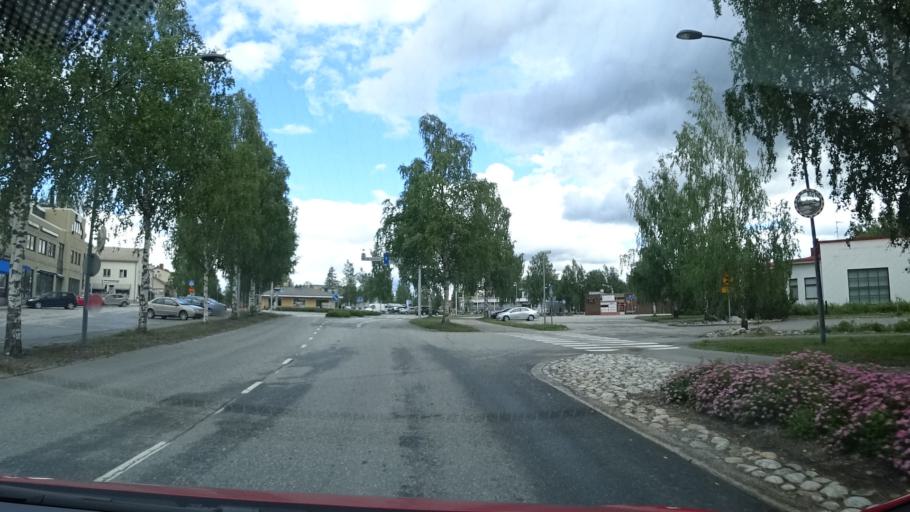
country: FI
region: North Karelia
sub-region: Pielisen Karjala
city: Nurmes
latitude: 63.5417
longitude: 29.1382
